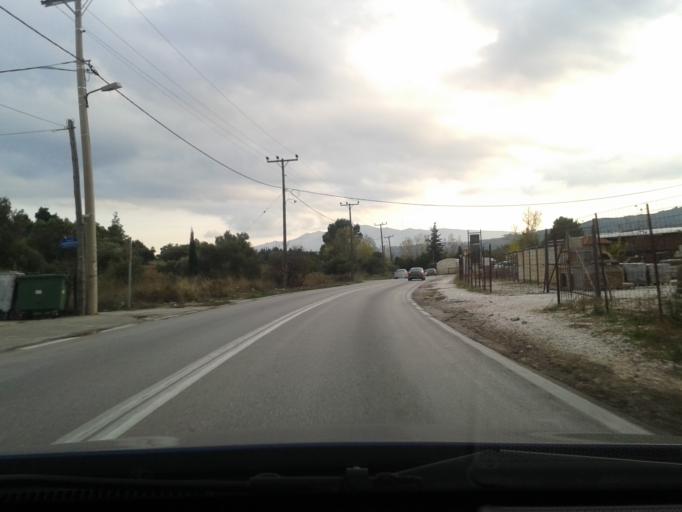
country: GR
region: Attica
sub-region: Nomarchia Anatolikis Attikis
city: Afidnes
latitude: 38.1931
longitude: 23.8539
